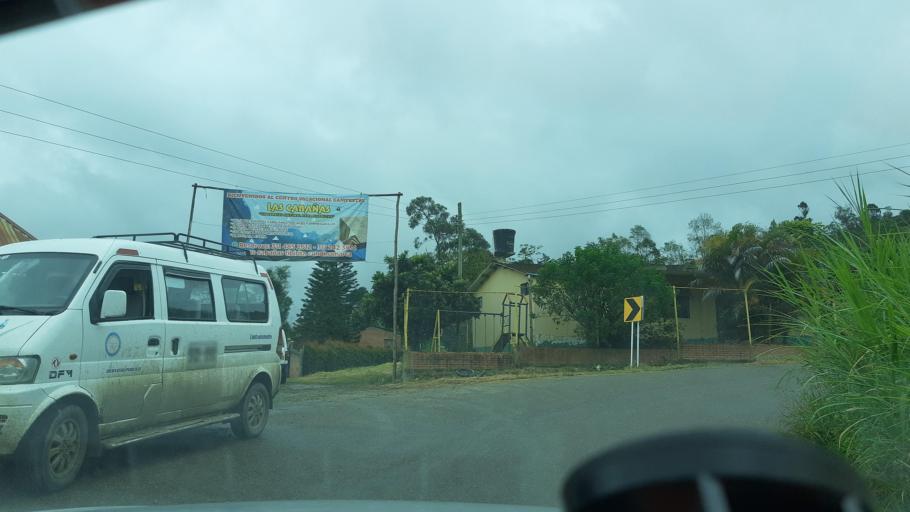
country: CO
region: Cundinamarca
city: Manta
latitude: 5.0421
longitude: -73.5126
